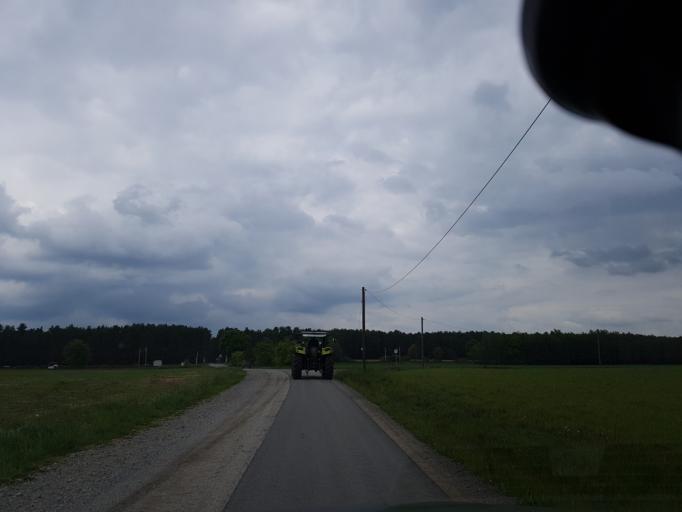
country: DE
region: Brandenburg
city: Crinitz
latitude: 51.6608
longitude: 13.7855
